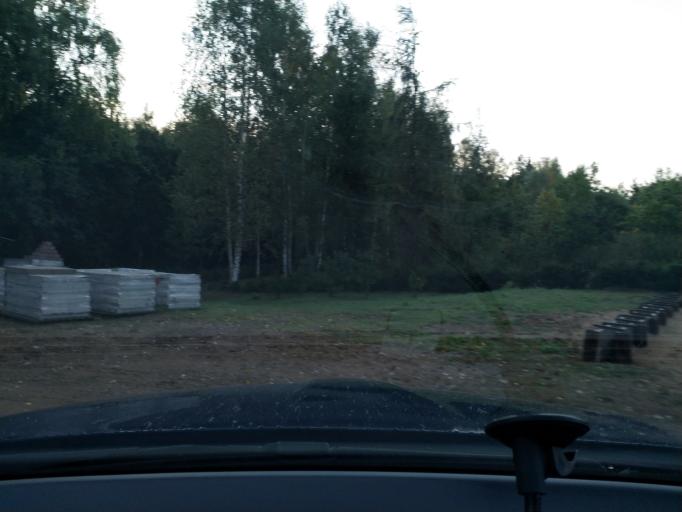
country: LV
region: Kuldigas Rajons
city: Kuldiga
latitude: 56.9792
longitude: 21.8802
